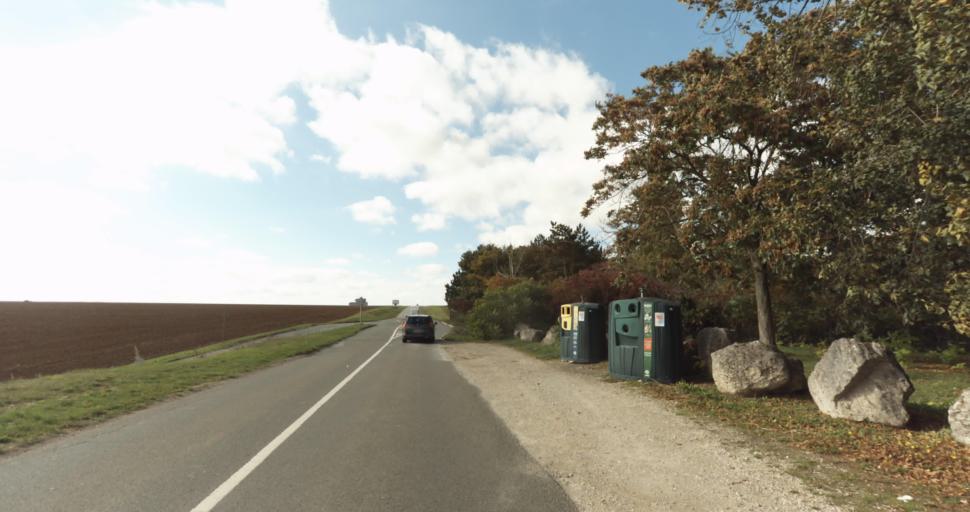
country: FR
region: Centre
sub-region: Departement d'Eure-et-Loir
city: Garnay
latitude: 48.7218
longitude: 1.3243
